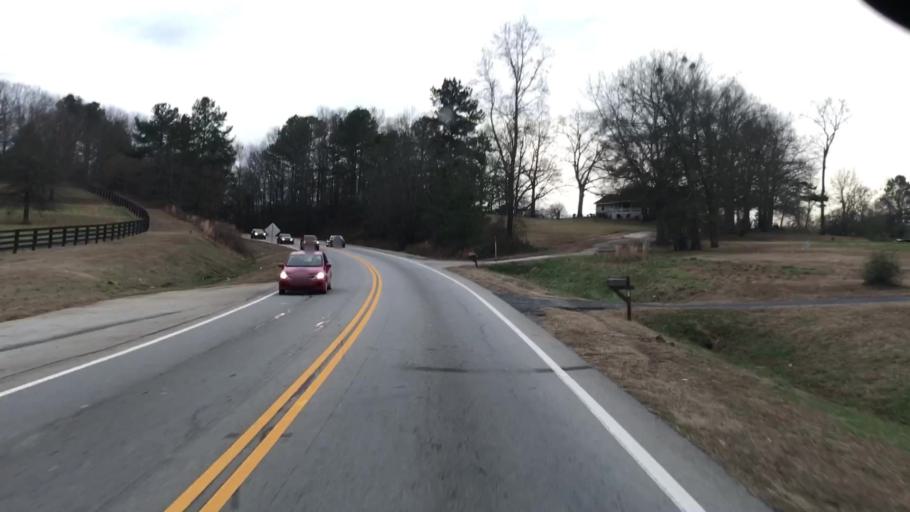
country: US
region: Georgia
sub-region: Jackson County
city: Hoschton
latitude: 34.0612
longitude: -83.7834
